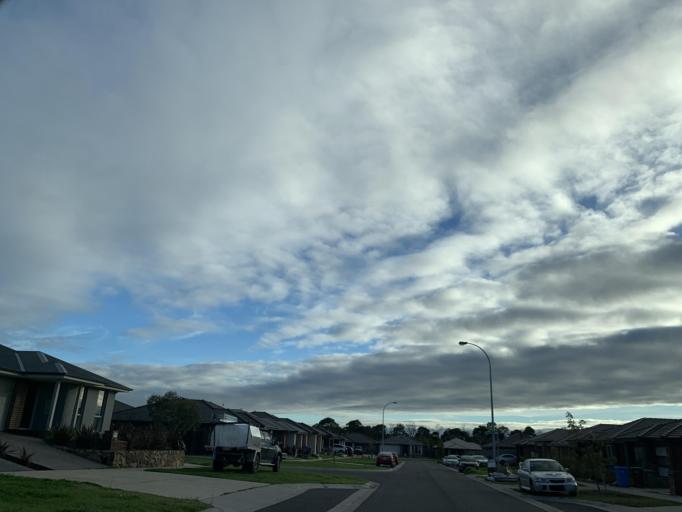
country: AU
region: Victoria
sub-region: Casey
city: Cranbourne East
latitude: -38.1270
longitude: 145.3218
